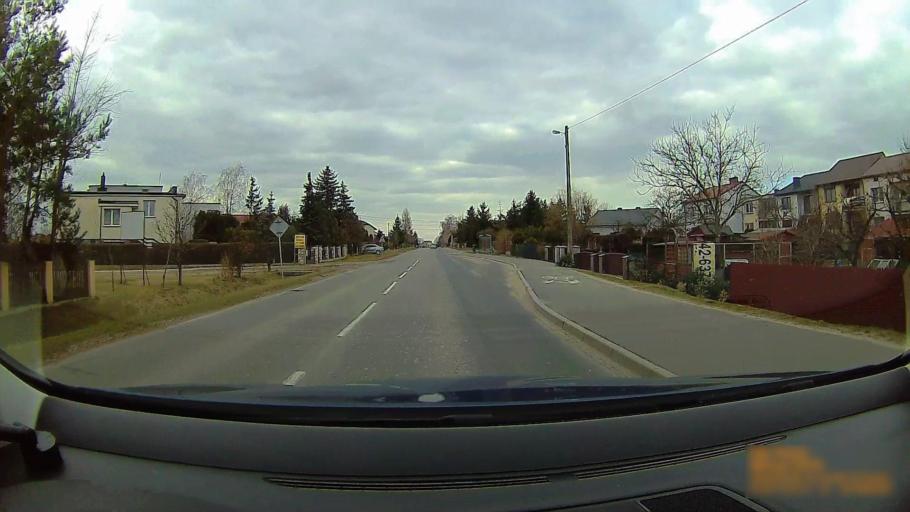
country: PL
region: Greater Poland Voivodeship
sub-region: Powiat koninski
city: Stare Miasto
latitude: 52.1993
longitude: 18.1521
